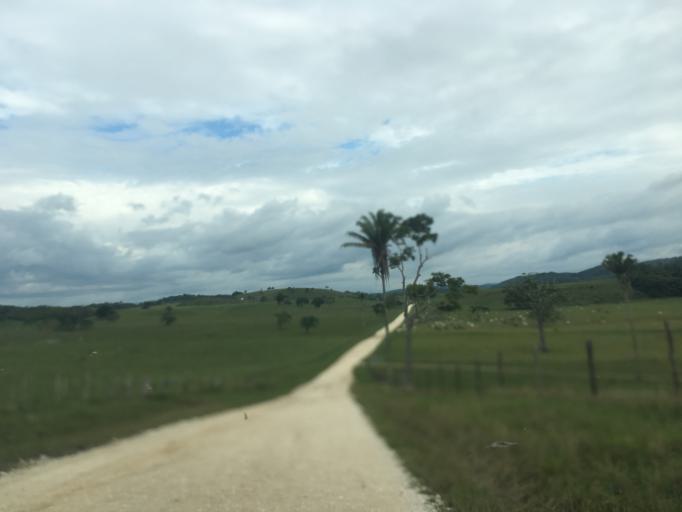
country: BZ
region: Cayo
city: Benque Viejo del Carmen
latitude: 17.1121
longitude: -89.1230
